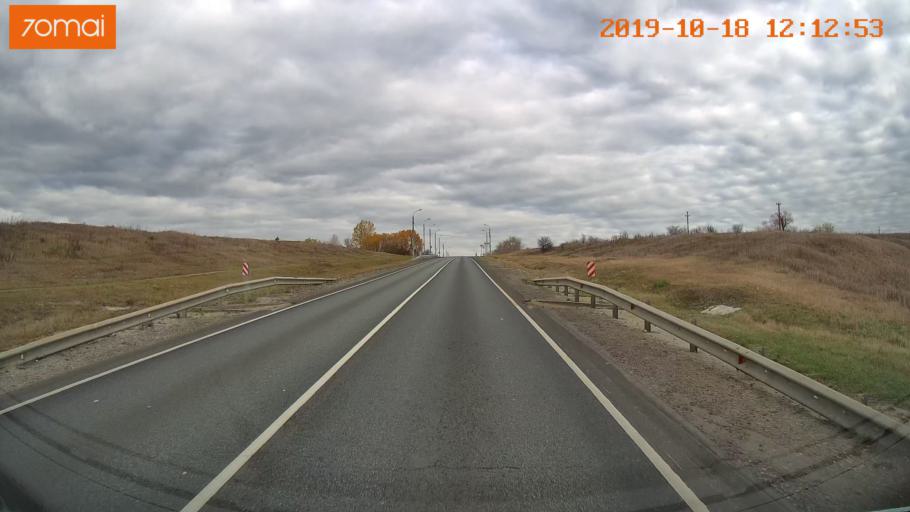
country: RU
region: Rjazan
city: Zakharovo
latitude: 54.4164
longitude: 39.3639
